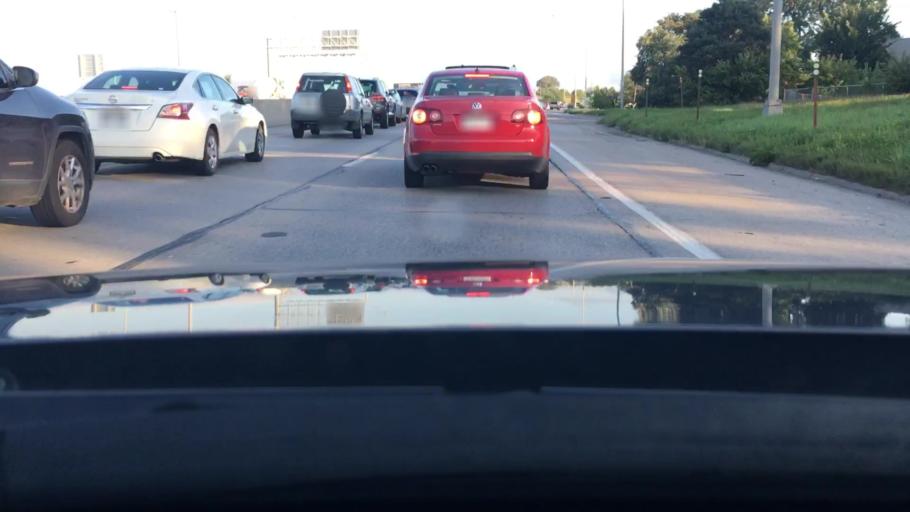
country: US
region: Nebraska
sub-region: Douglas County
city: Omaha
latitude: 41.2138
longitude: -95.9516
